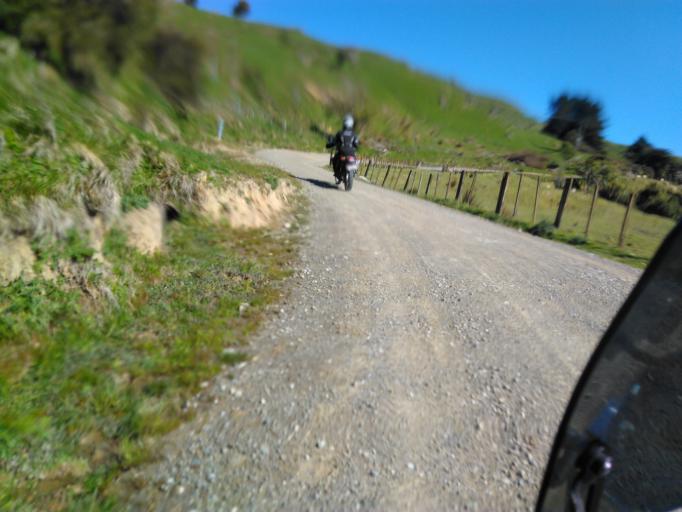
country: NZ
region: Bay of Plenty
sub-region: Opotiki District
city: Opotiki
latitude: -38.3630
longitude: 177.5944
